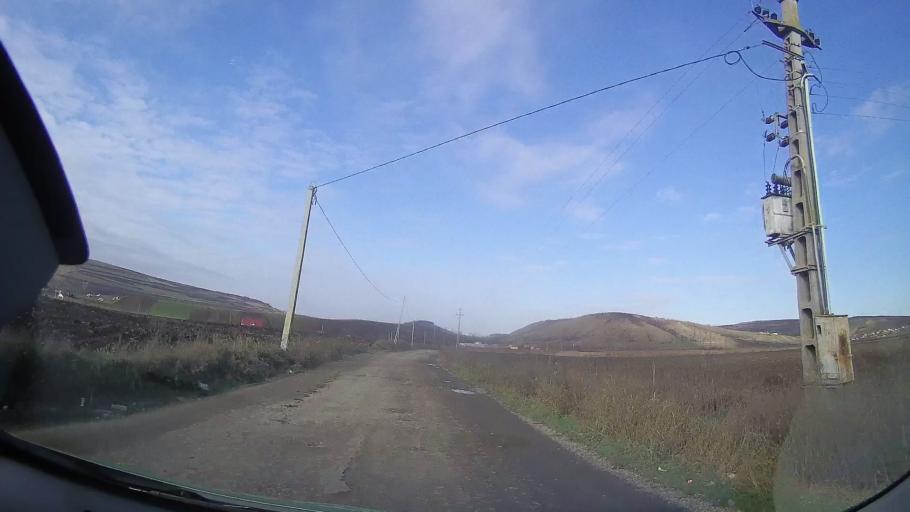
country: RO
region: Mures
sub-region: Comuna Zau De Campie
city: Zau de Campie
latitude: 46.5939
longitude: 24.1088
